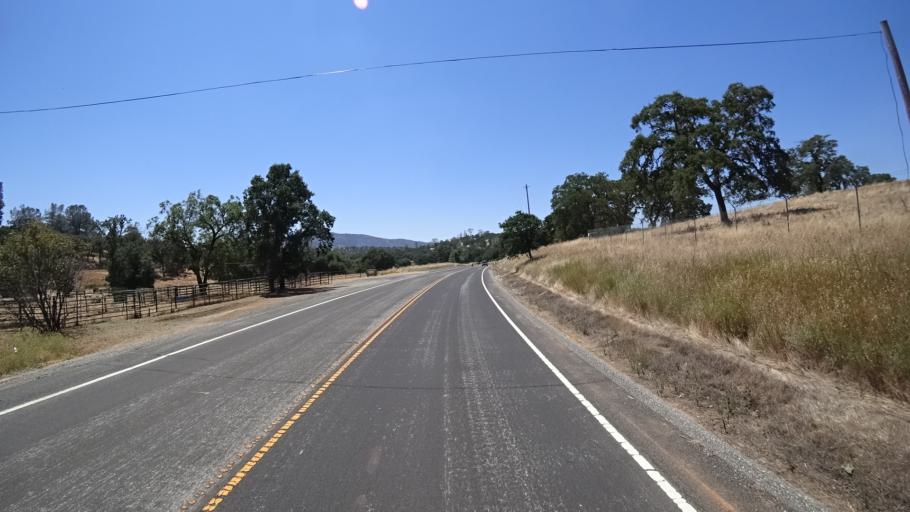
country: US
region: California
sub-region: Calaveras County
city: Angels Camp
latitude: 38.0447
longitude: -120.5280
